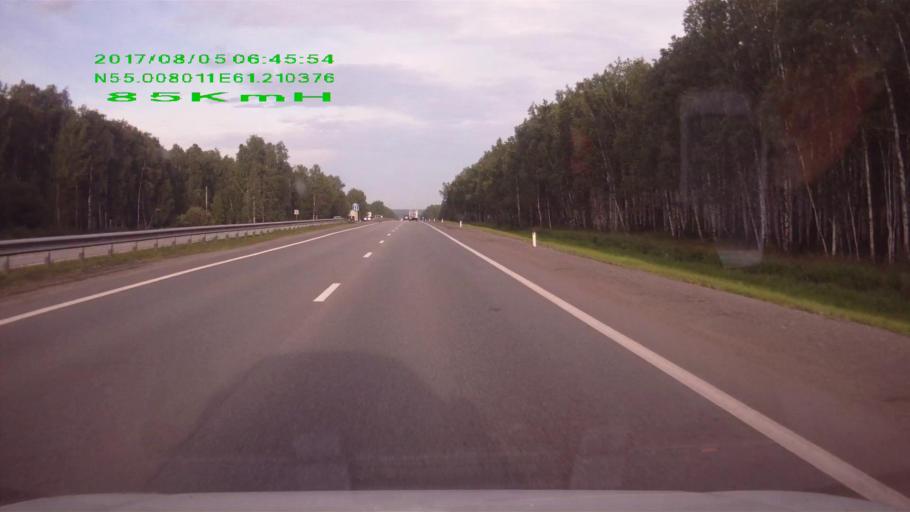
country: RU
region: Chelyabinsk
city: Sargazy
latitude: 55.0080
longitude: 61.2100
